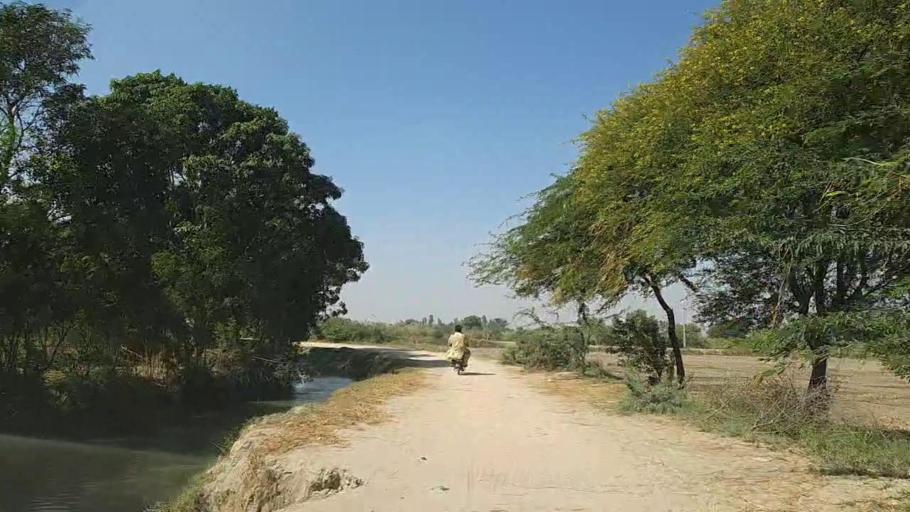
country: PK
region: Sindh
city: Daro Mehar
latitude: 24.7916
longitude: 68.1738
